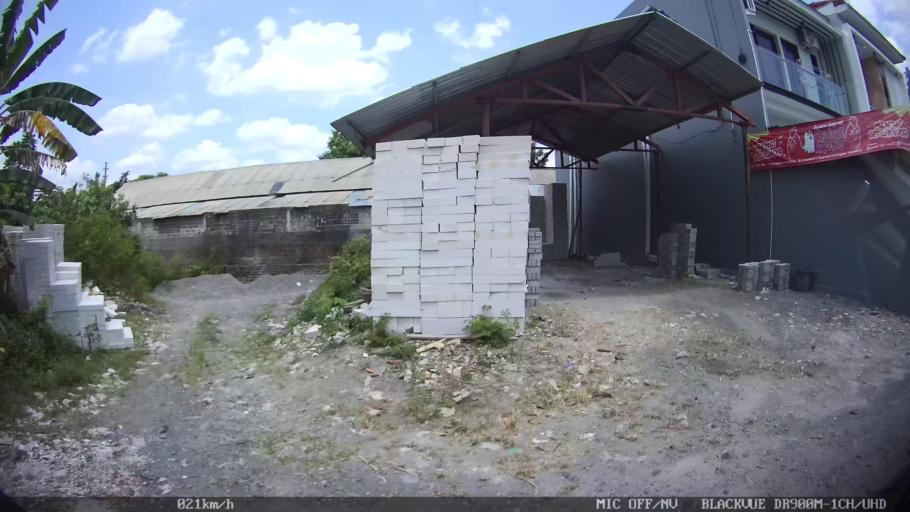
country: ID
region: Daerah Istimewa Yogyakarta
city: Kasihan
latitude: -7.8111
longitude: 110.3438
